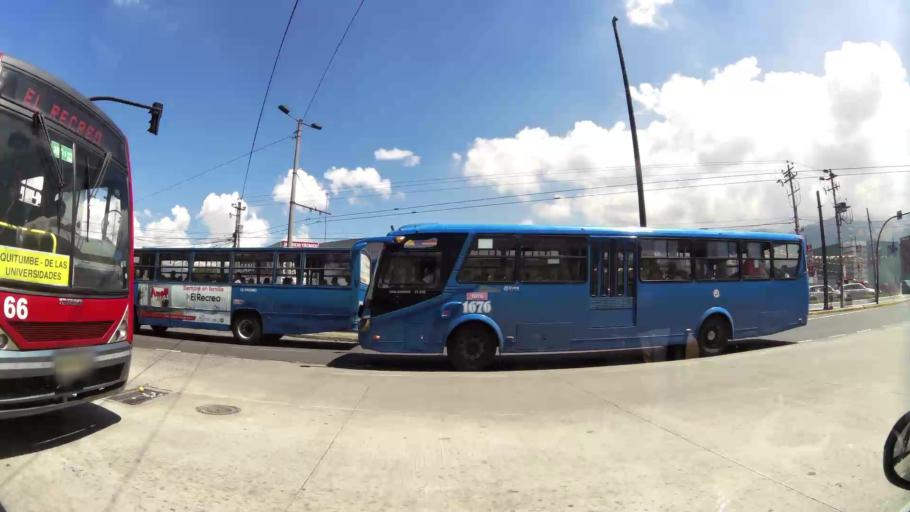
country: EC
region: Pichincha
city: Quito
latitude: -0.2545
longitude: -78.5223
